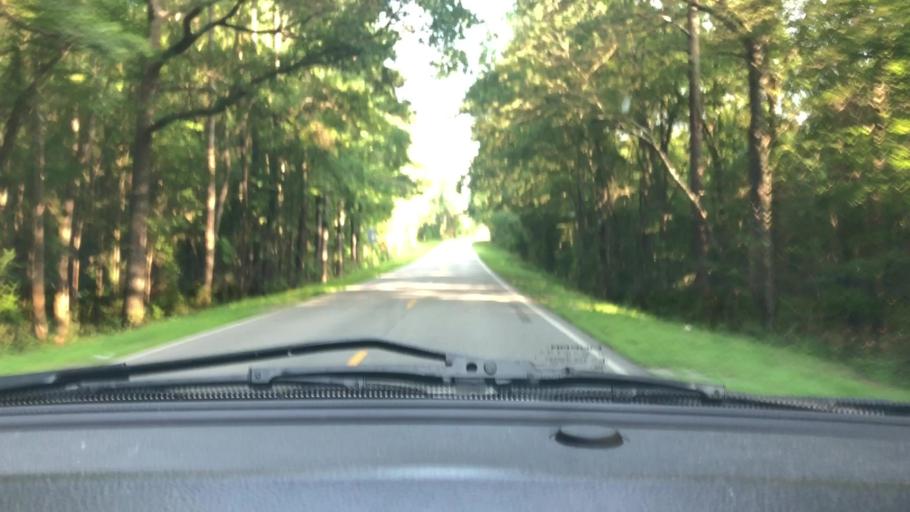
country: US
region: North Carolina
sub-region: Lee County
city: Broadway
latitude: 35.3335
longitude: -79.0725
